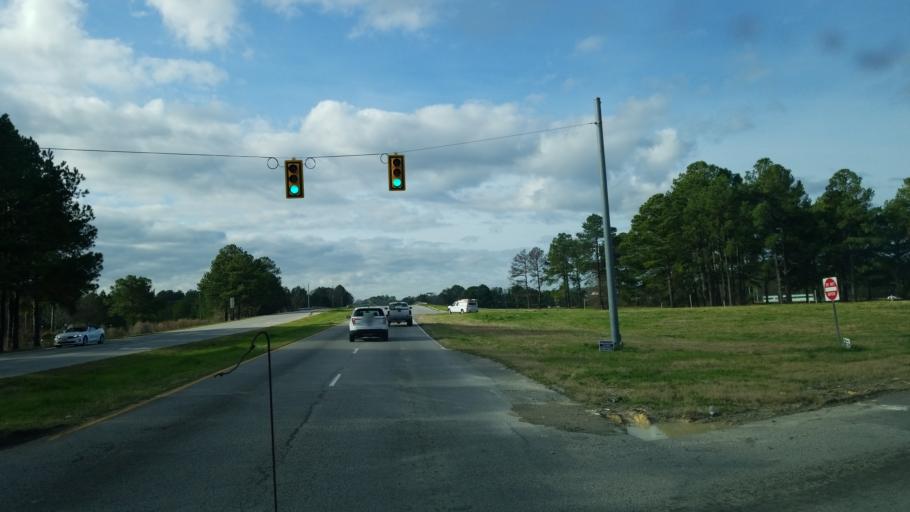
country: US
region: South Carolina
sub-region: Richland County
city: Dentsville
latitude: 34.1025
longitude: -80.9567
